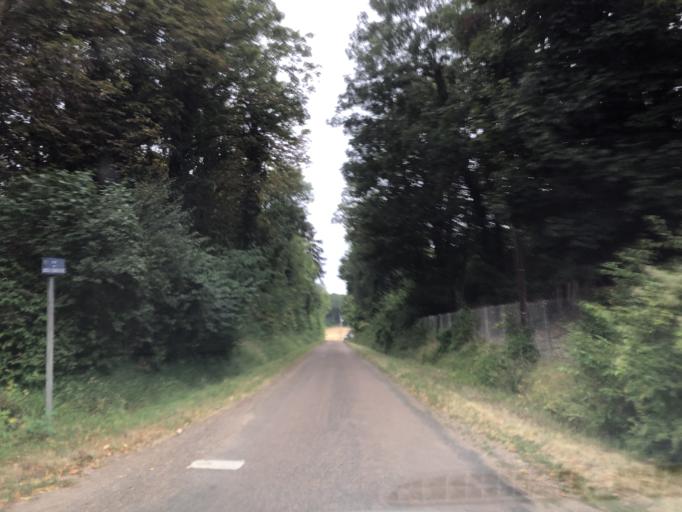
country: FR
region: Bourgogne
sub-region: Departement de l'Yonne
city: Aillant-sur-Tholon
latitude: 47.9037
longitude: 3.3238
